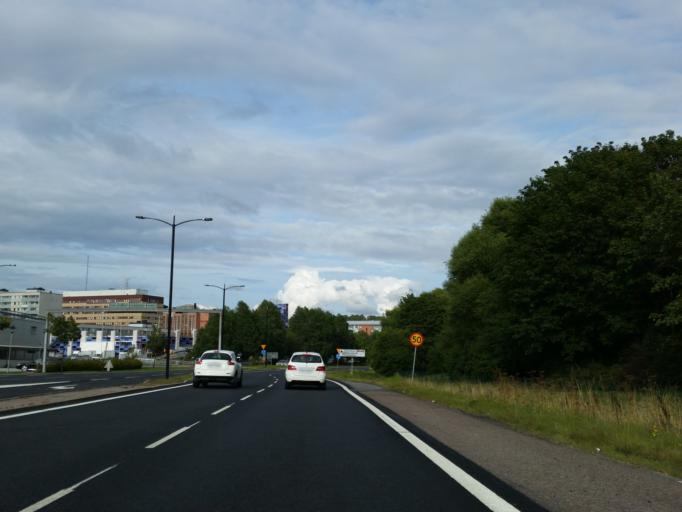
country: SE
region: Stockholm
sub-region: Sollentuna Kommun
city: Sollentuna
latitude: 59.4227
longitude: 17.9466
